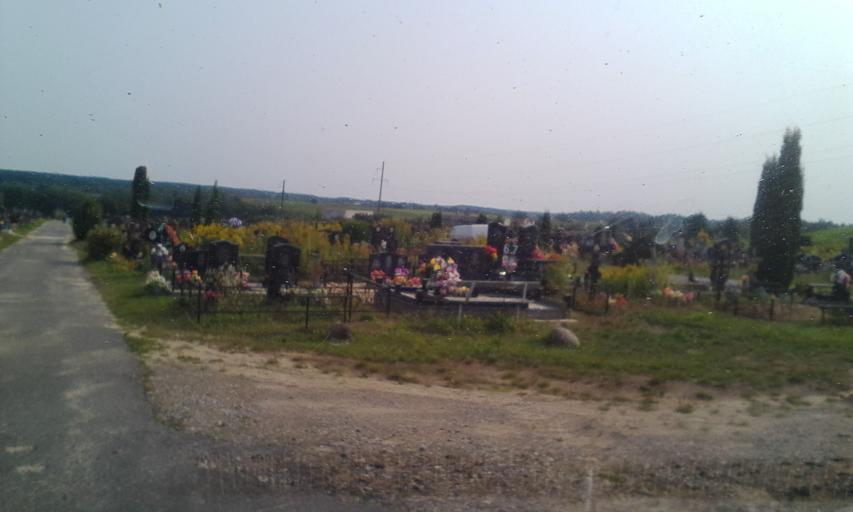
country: BY
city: Michanovichi
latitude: 53.7661
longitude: 27.7005
